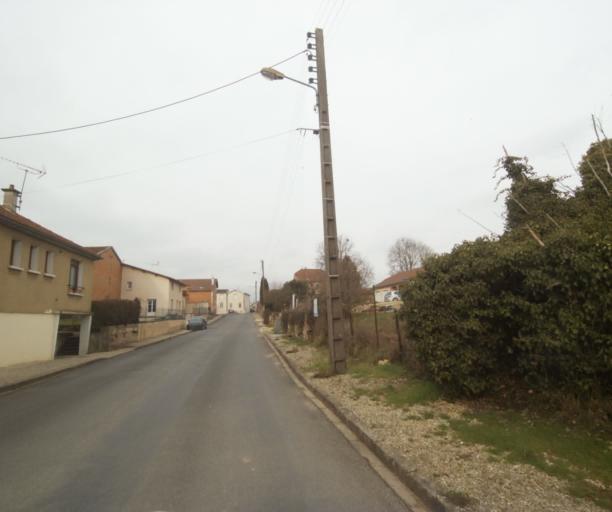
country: FR
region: Champagne-Ardenne
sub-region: Departement de la Marne
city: Pargny-sur-Saulx
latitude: 48.7497
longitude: 4.8532
